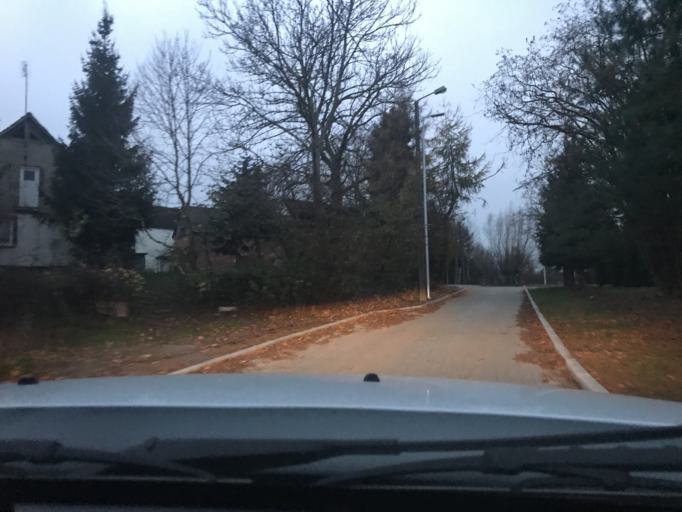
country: PL
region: West Pomeranian Voivodeship
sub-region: Powiat slawienski
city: Darlowo
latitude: 54.4771
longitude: 16.5117
